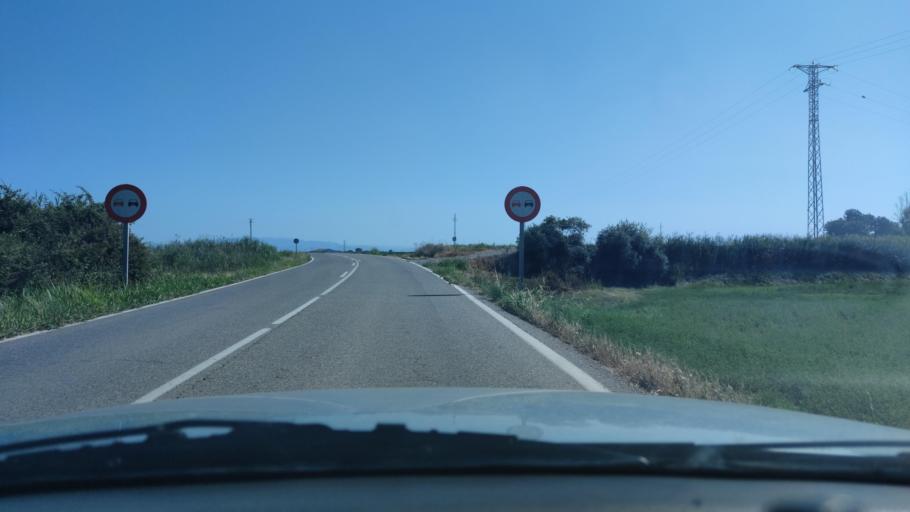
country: ES
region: Catalonia
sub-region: Provincia de Lleida
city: Sidamon
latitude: 41.6404
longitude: 0.7939
